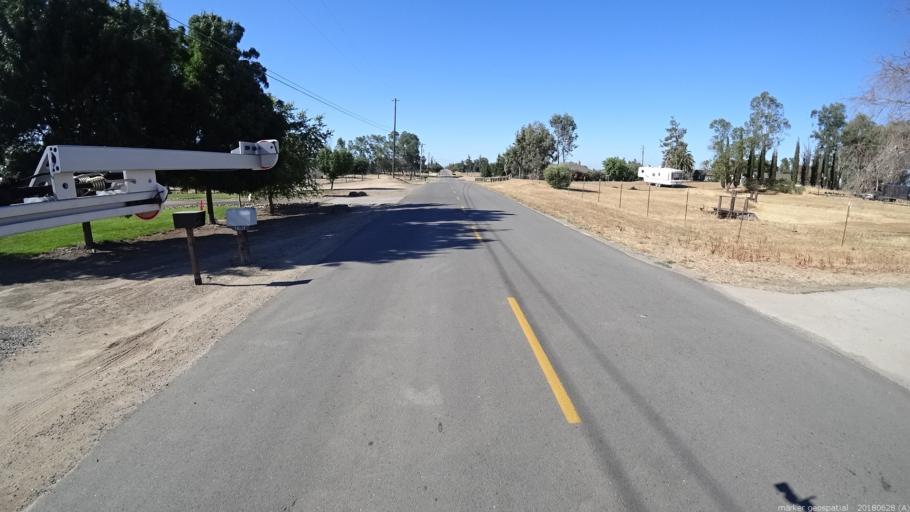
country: US
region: California
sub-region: Madera County
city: Bonadelle Ranchos-Madera Ranchos
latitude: 36.9855
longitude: -119.8901
